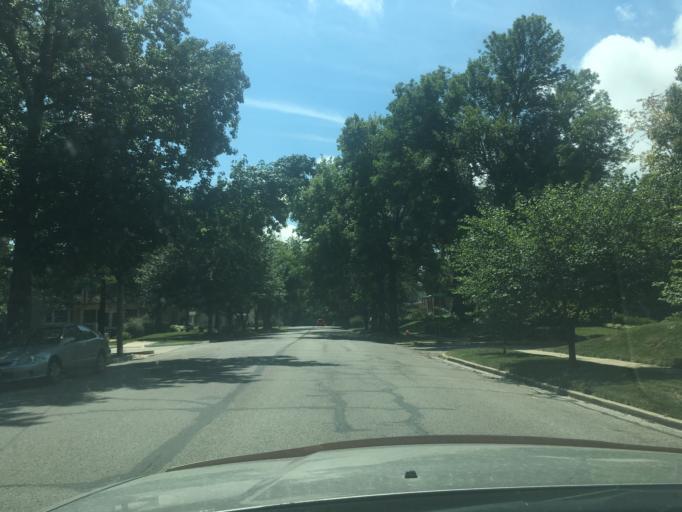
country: US
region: Kansas
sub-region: Atchison County
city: Atchison
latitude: 39.5687
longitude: -95.1190
